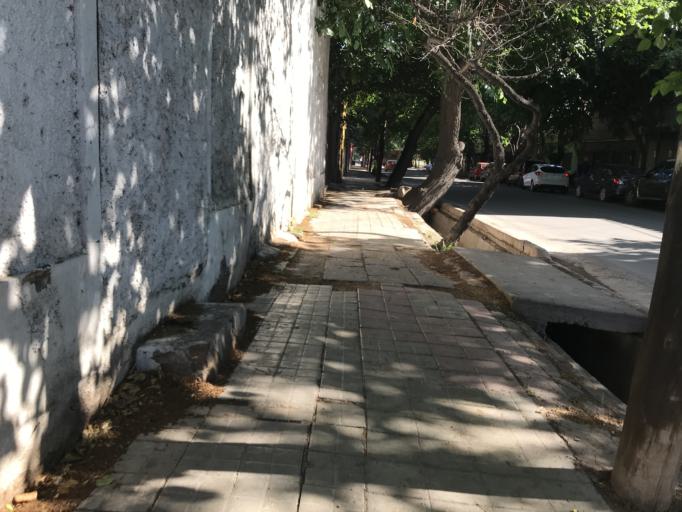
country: AR
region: Mendoza
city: Mendoza
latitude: -32.8862
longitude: -68.8313
